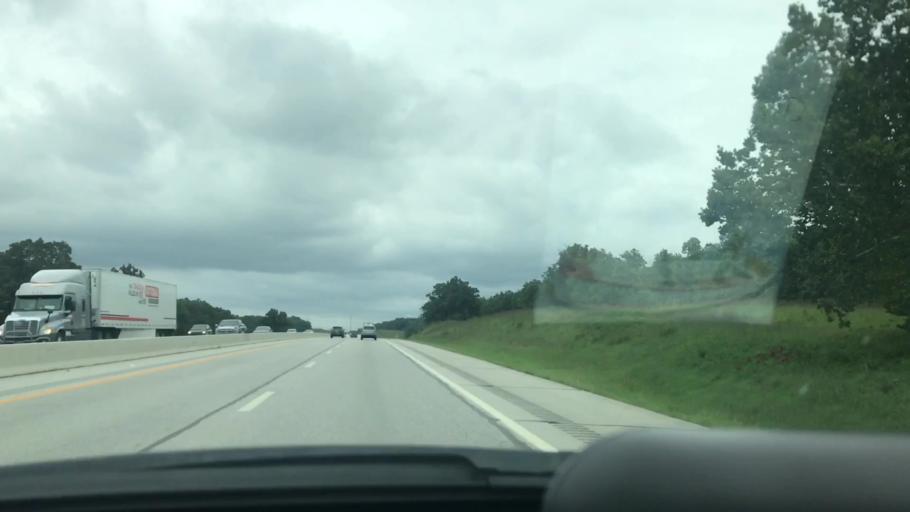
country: US
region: Kansas
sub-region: Cherokee County
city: Baxter Springs
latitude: 36.9727
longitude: -94.6466
